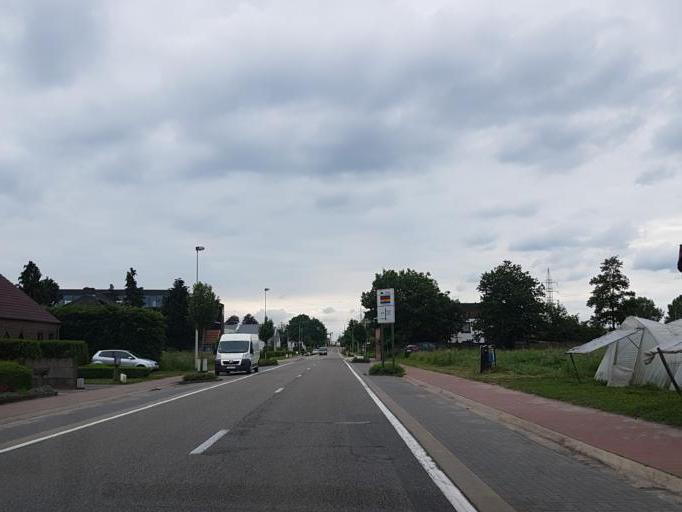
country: BE
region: Flanders
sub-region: Provincie Antwerpen
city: Rijkevorsel
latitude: 51.3342
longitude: 4.7494
